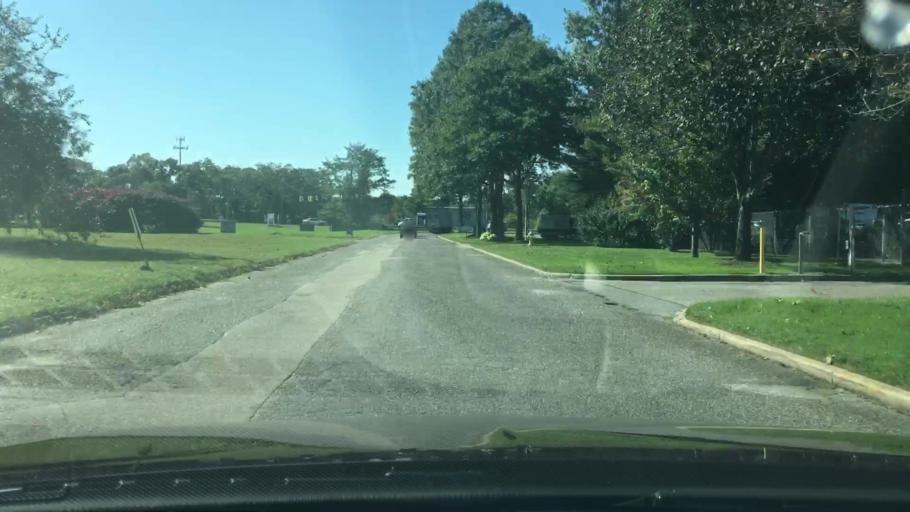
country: US
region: New York
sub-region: Suffolk County
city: Yaphank
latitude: 40.8411
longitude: -72.8863
